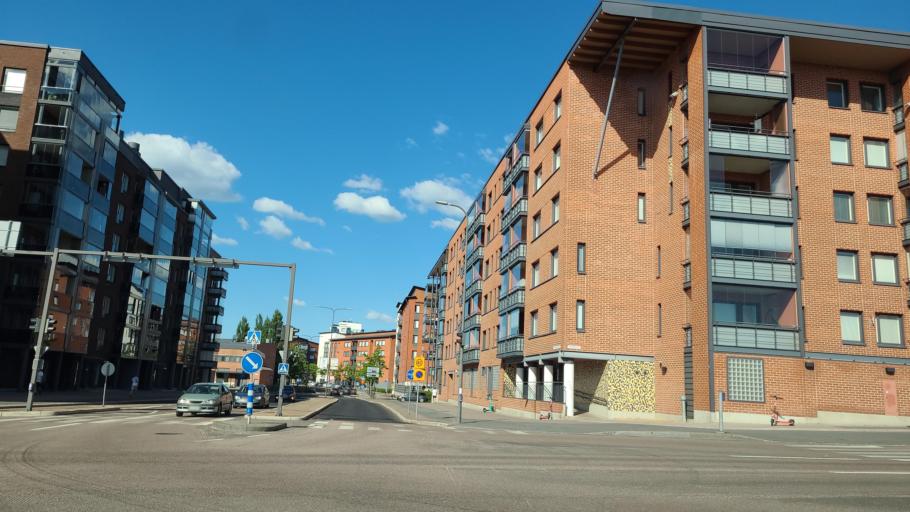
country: FI
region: Central Finland
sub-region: Jyvaeskylae
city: Jyvaeskylae
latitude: 62.2368
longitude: 25.7581
